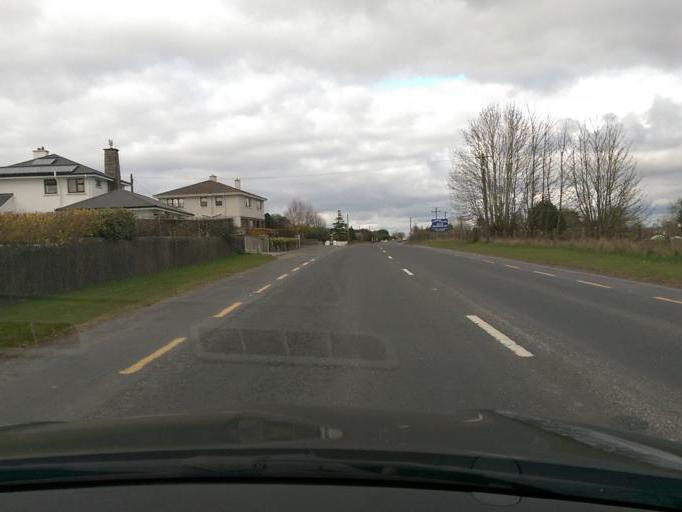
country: IE
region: Leinster
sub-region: An Iarmhi
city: Athlone
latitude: 53.3983
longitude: -7.9893
